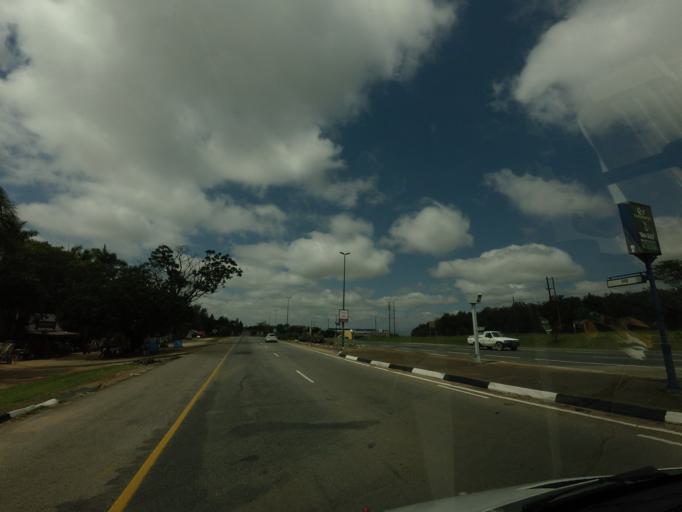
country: ZA
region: Mpumalanga
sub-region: Ehlanzeni District
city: White River
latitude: -25.3382
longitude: 31.0009
